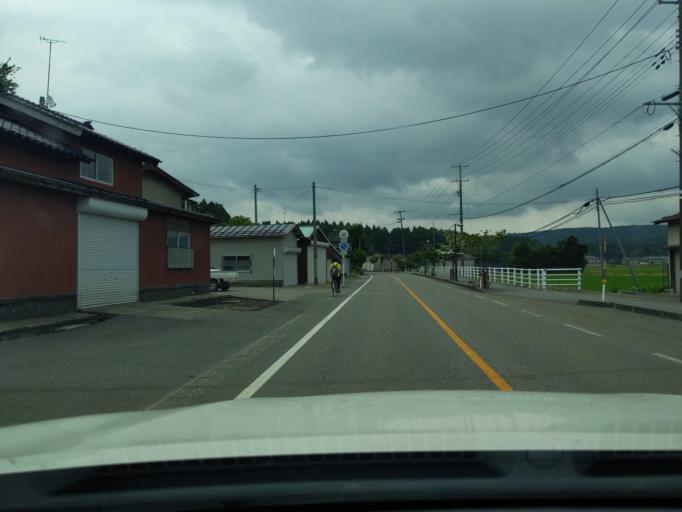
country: JP
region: Niigata
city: Kashiwazaki
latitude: 37.3388
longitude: 138.5723
